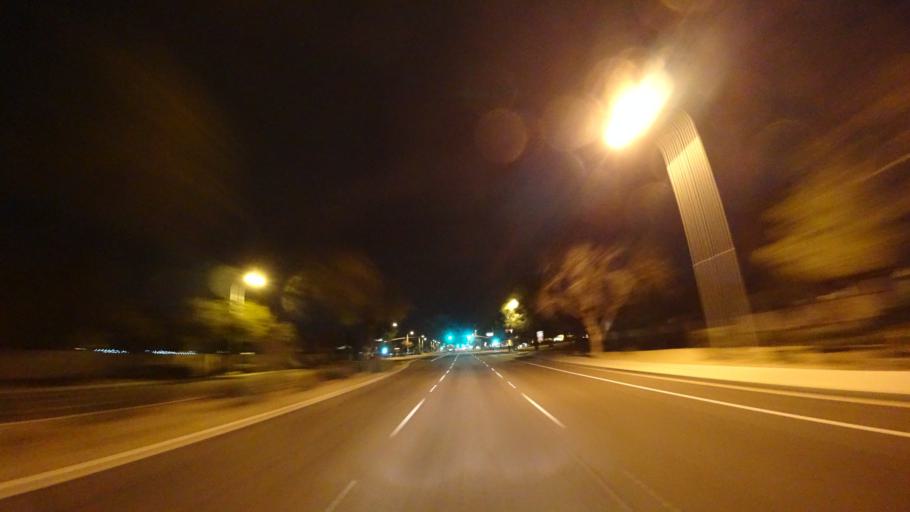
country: US
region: Arizona
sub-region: Maricopa County
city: Chandler
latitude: 33.3063
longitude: -111.8127
